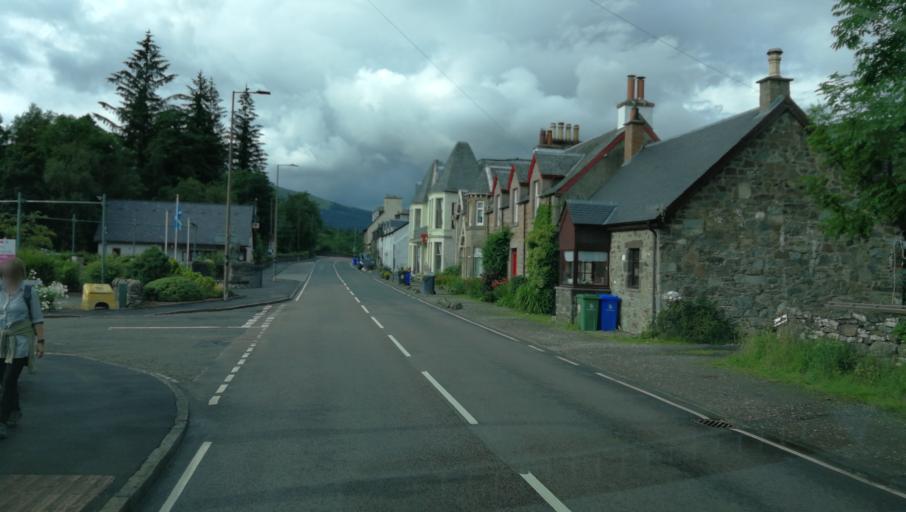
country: GB
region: Scotland
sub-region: Stirling
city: Callander
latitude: 56.3238
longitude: -4.3286
